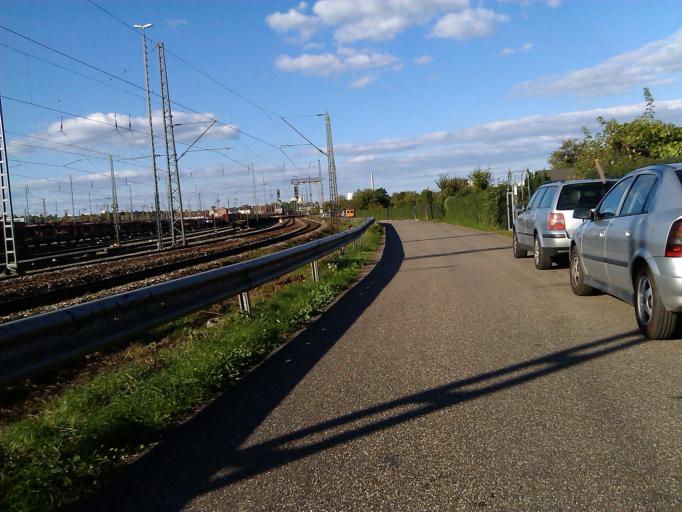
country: DE
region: Baden-Wuerttemberg
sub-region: Regierungsbezirk Stuttgart
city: Heilbronn
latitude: 49.1335
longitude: 9.1967
